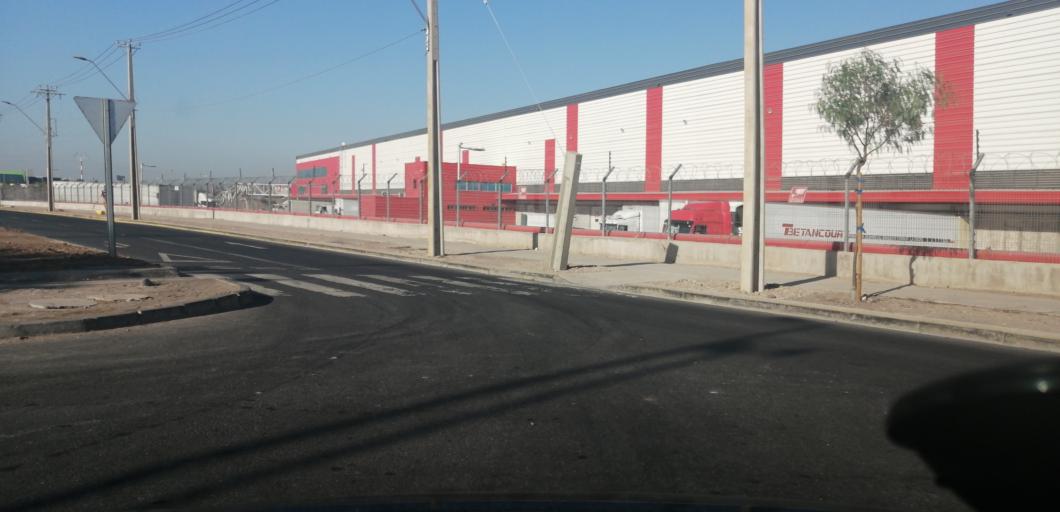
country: CL
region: Santiago Metropolitan
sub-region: Provincia de Santiago
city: Lo Prado
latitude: -33.4349
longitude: -70.7882
